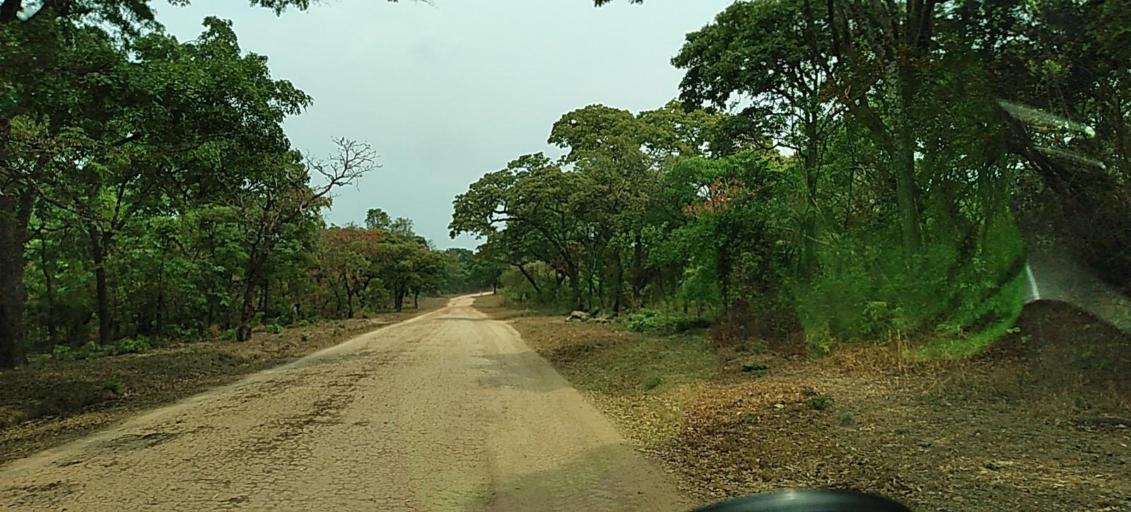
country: ZM
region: North-Western
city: Solwezi
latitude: -12.8234
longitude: 26.5372
